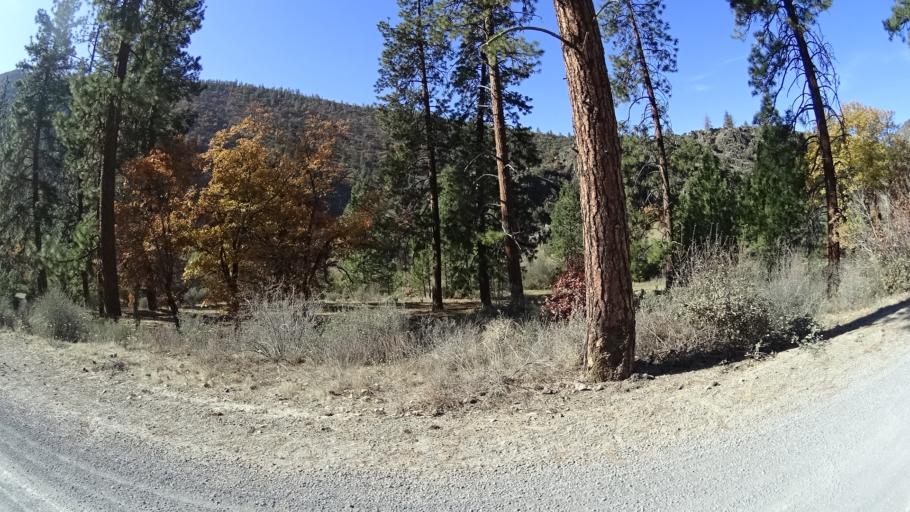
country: US
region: California
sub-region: Siskiyou County
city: Yreka
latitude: 41.8270
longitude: -122.6564
